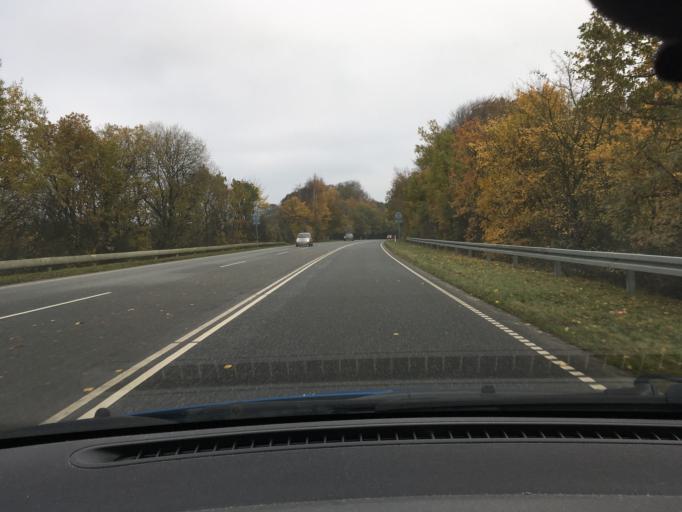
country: DK
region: South Denmark
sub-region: Aabenraa Kommune
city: Aabenraa
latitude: 55.0100
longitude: 9.4208
